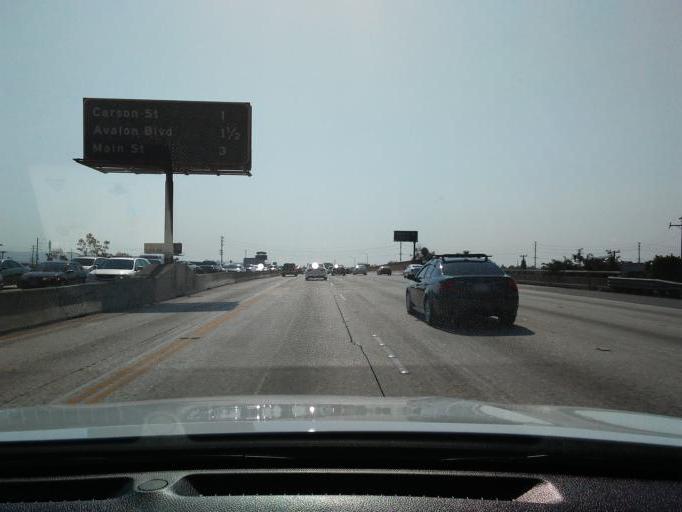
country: US
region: California
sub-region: Los Angeles County
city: Carson
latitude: 33.8260
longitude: -118.2409
